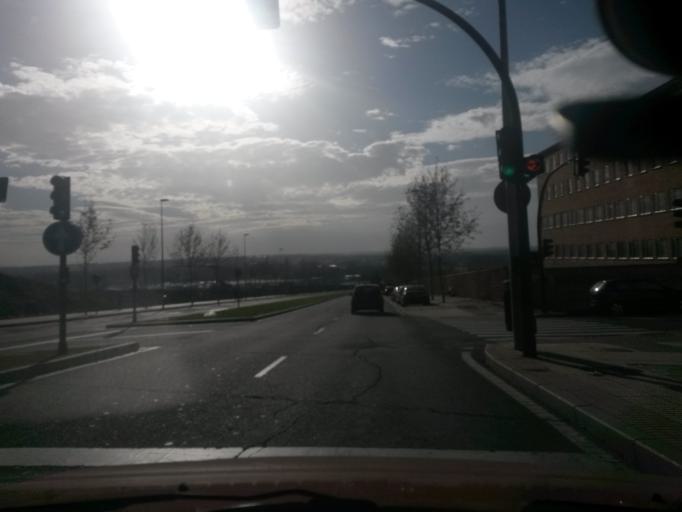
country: ES
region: Castille and Leon
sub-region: Provincia de Salamanca
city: Salamanca
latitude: 40.9681
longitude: -5.6436
